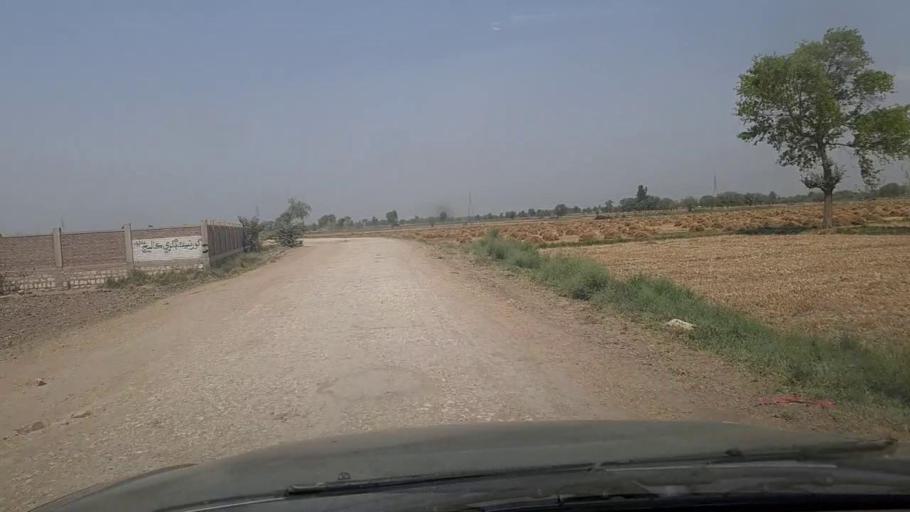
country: PK
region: Sindh
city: Adilpur
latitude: 27.9400
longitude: 69.3115
